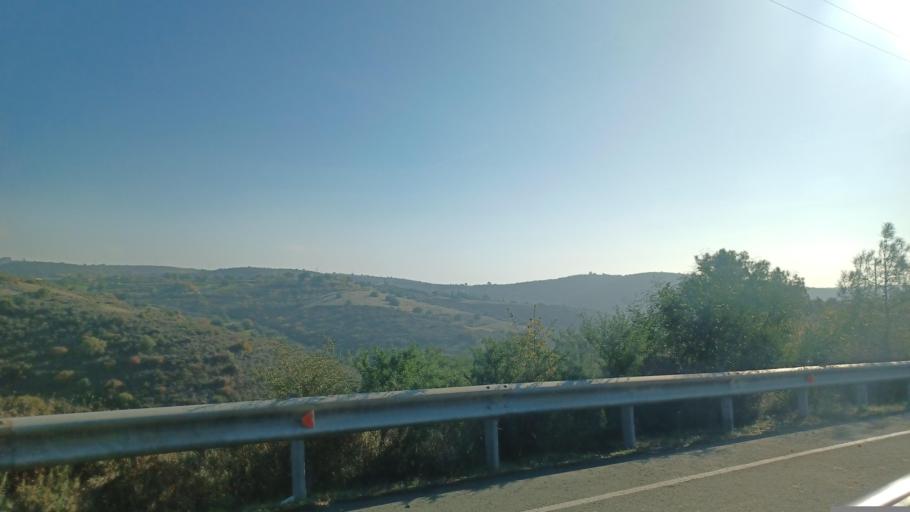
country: CY
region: Larnaka
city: Kofinou
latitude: 34.8446
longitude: 33.3003
